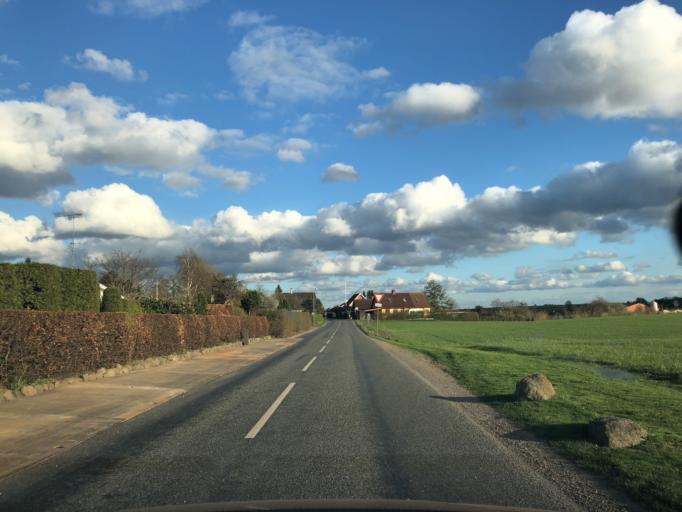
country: DK
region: Zealand
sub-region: Ringsted Kommune
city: Ringsted
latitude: 55.4955
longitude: 11.8634
